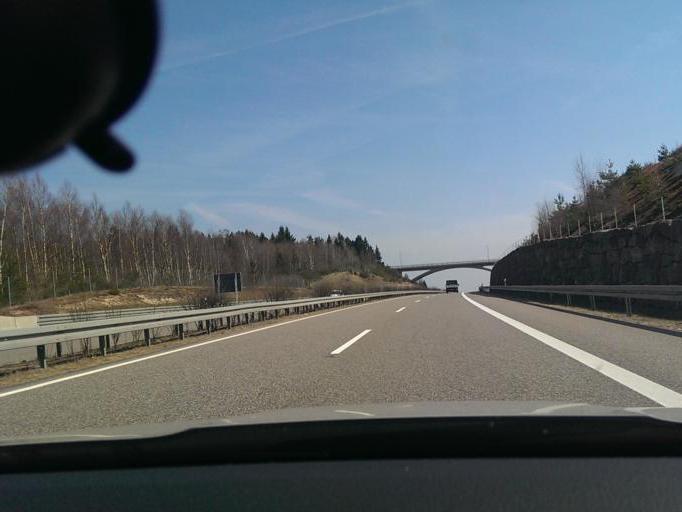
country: DE
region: Thuringia
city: Suhl
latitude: 50.5829
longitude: 10.7063
